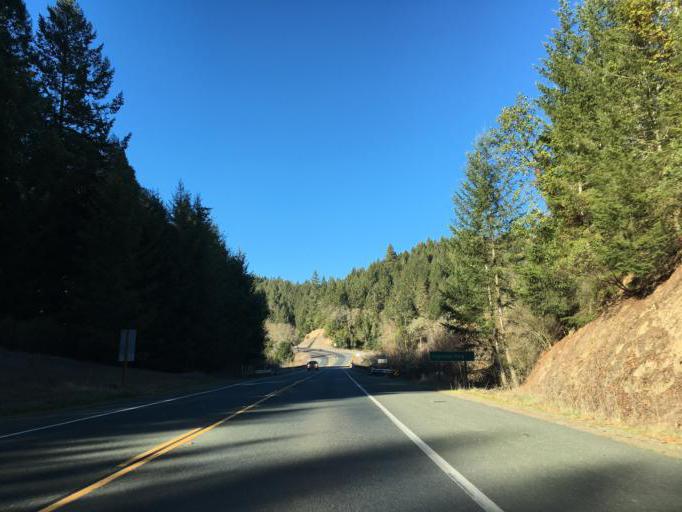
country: US
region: California
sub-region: Mendocino County
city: Brooktrails
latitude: 39.4617
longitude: -123.3501
